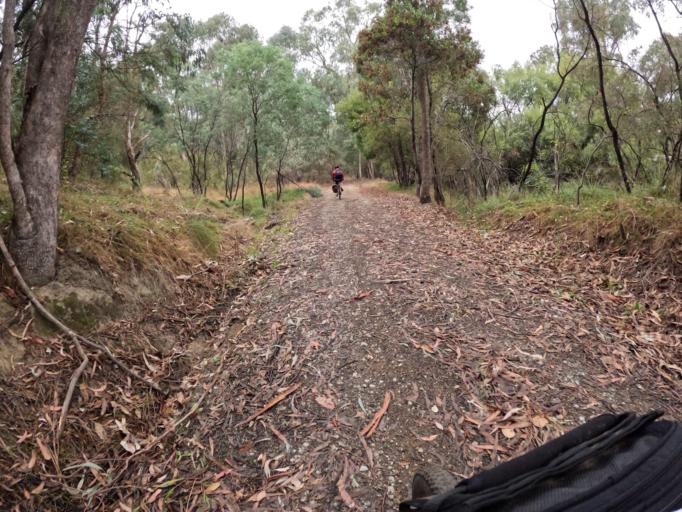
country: AU
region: New South Wales
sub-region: Greater Hume Shire
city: Holbrook
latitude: -36.1660
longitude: 147.4054
